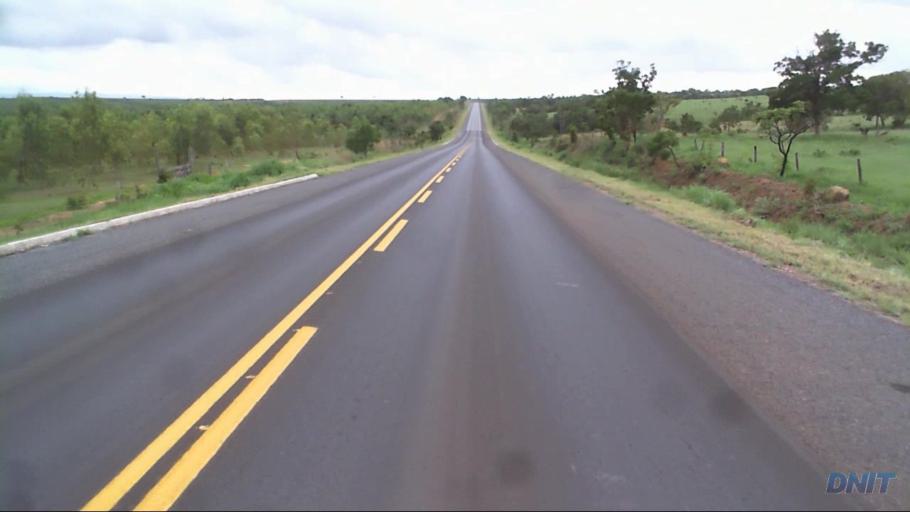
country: BR
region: Goias
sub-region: Barro Alto
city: Barro Alto
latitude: -15.2139
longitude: -48.6610
